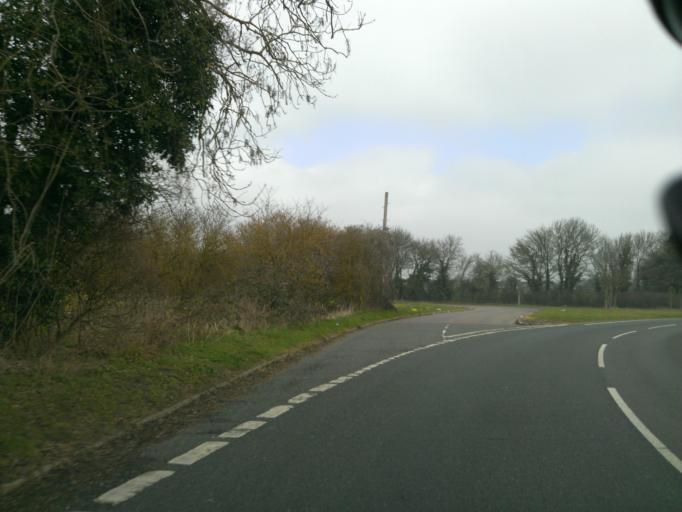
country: GB
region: England
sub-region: Essex
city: Rayne
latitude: 51.8428
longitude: 0.6132
